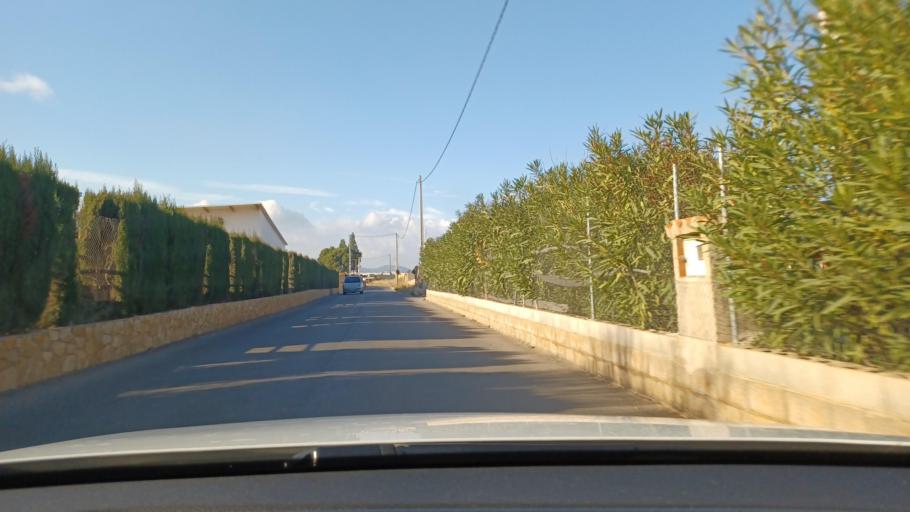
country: ES
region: Valencia
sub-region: Provincia de Castello
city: Onda
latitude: 39.9494
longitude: -0.2257
